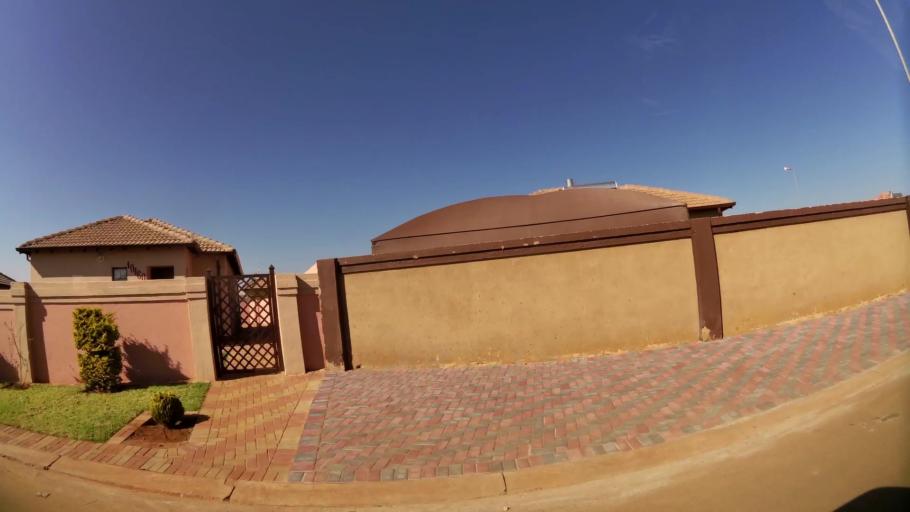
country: ZA
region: North-West
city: Ga-Rankuwa
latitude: -25.6389
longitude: 28.0761
